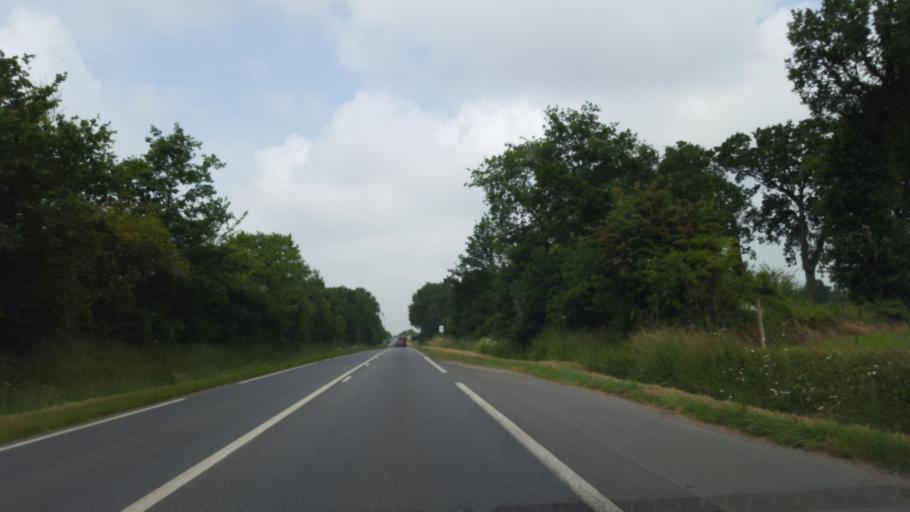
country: FR
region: Brittany
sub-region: Departement d'Ille-et-Vilaine
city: Chartres-de-Bretagne
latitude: 48.0441
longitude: -1.6985
